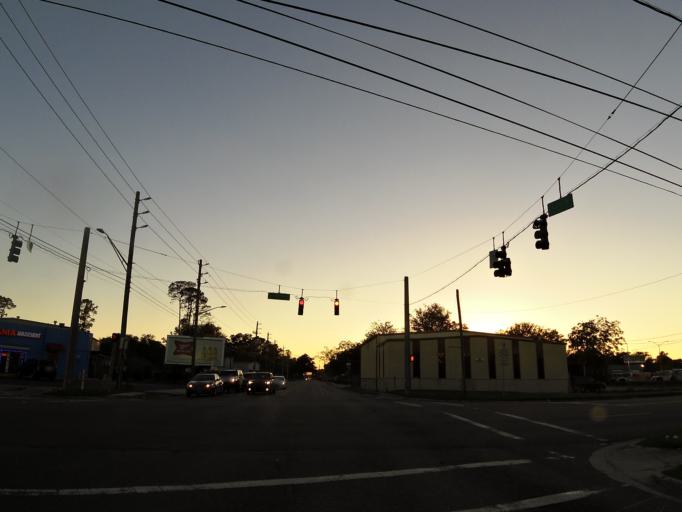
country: US
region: Florida
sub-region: Duval County
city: Jacksonville
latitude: 30.3181
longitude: -81.7245
